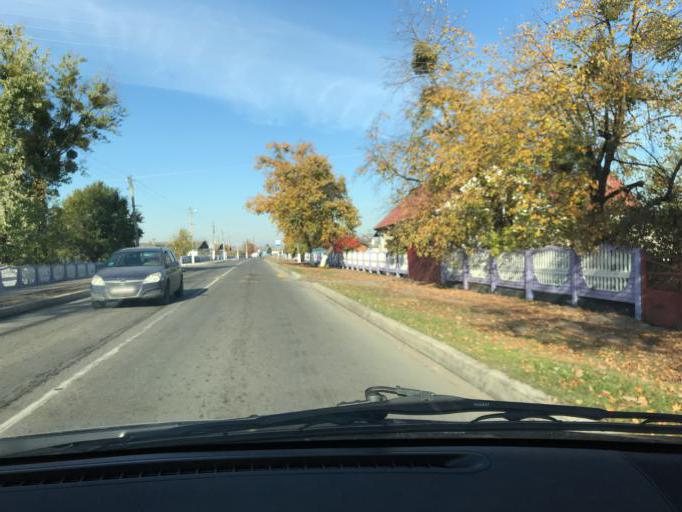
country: BY
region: Brest
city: Mikashevichy
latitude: 52.2228
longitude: 27.4646
